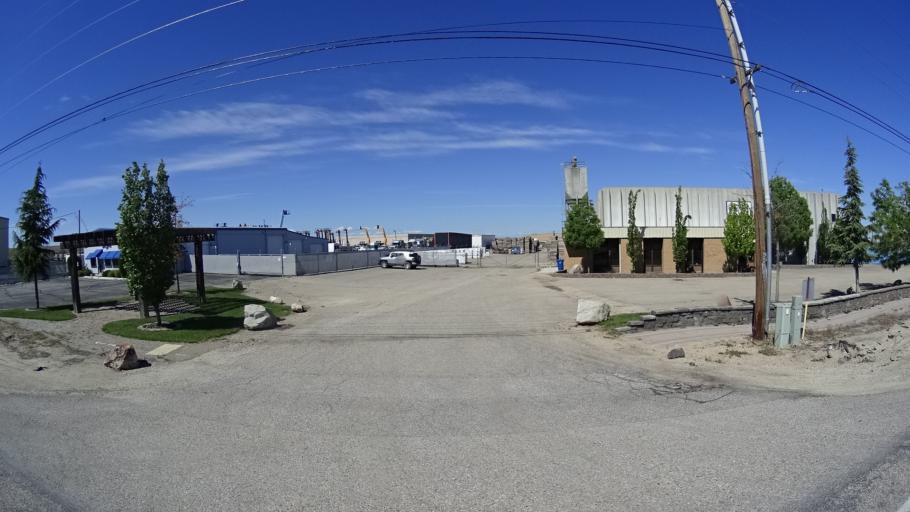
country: US
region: Idaho
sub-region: Ada County
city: Boise
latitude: 43.5345
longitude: -116.1529
